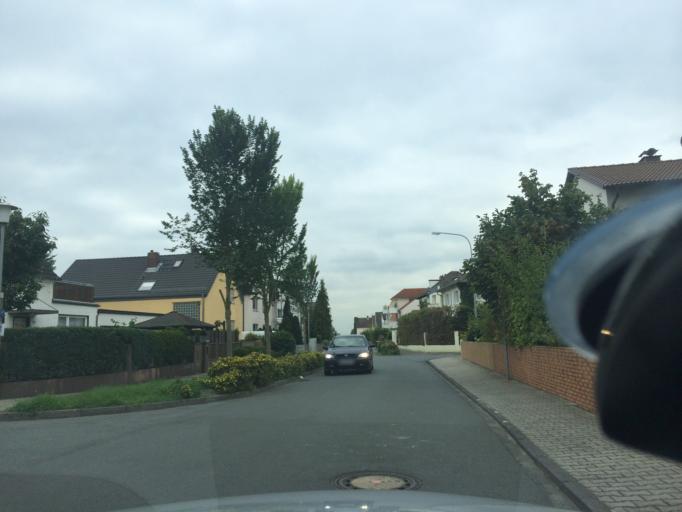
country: DE
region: Hesse
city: Morfelden-Walldorf
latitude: 49.9980
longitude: 8.5856
